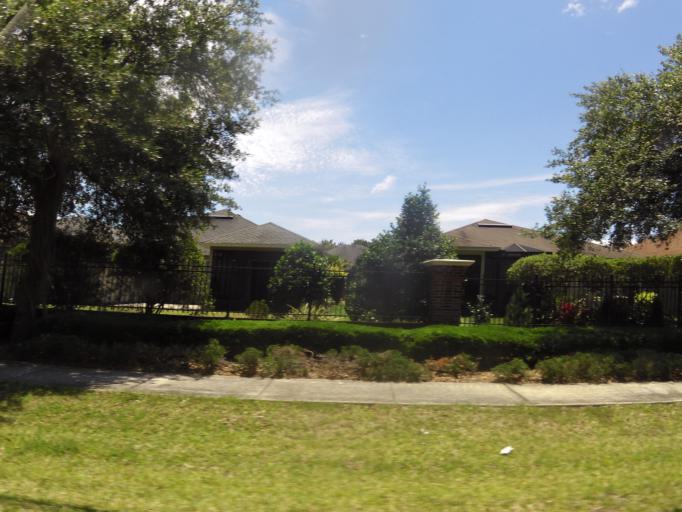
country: US
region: Florida
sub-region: Duval County
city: Jacksonville
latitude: 30.4642
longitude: -81.5564
